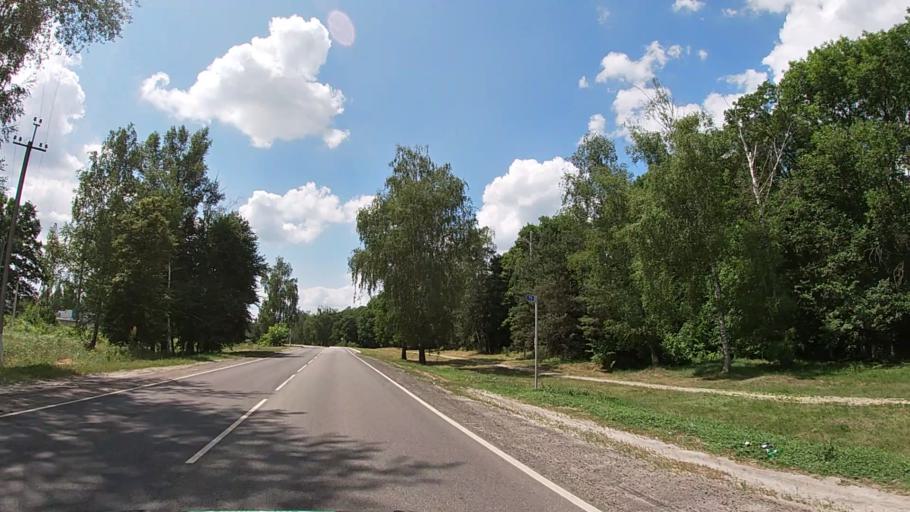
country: RU
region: Belgorod
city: Grayvoron
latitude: 50.4903
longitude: 35.6963
